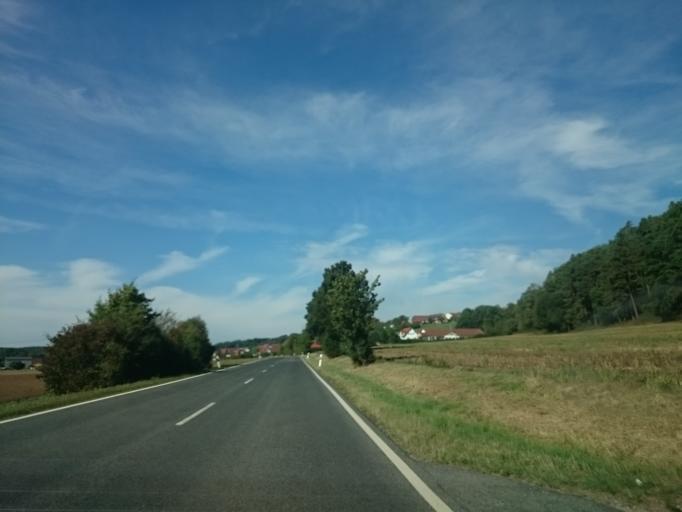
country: DE
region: Bavaria
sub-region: Regierungsbezirk Mittelfranken
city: Heideck
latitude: 49.1324
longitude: 11.0989
